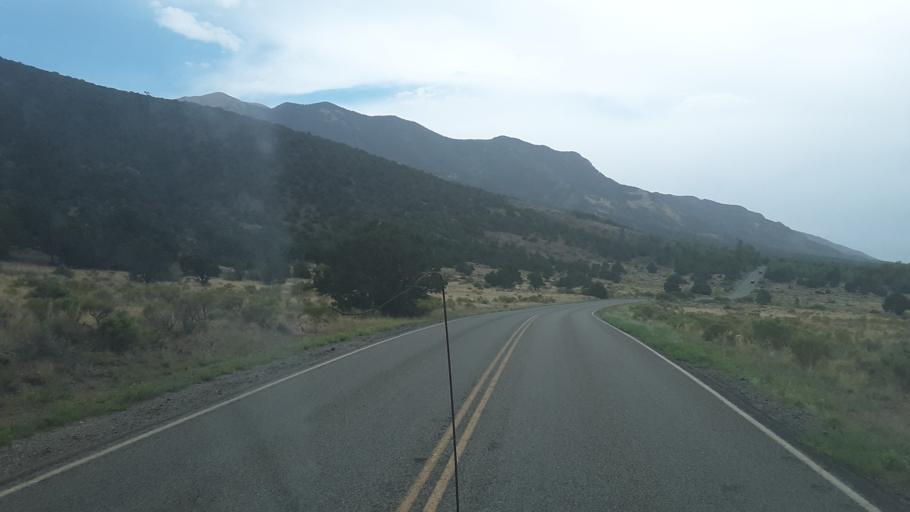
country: US
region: Colorado
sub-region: Custer County
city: Westcliffe
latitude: 37.7401
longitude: -105.5071
